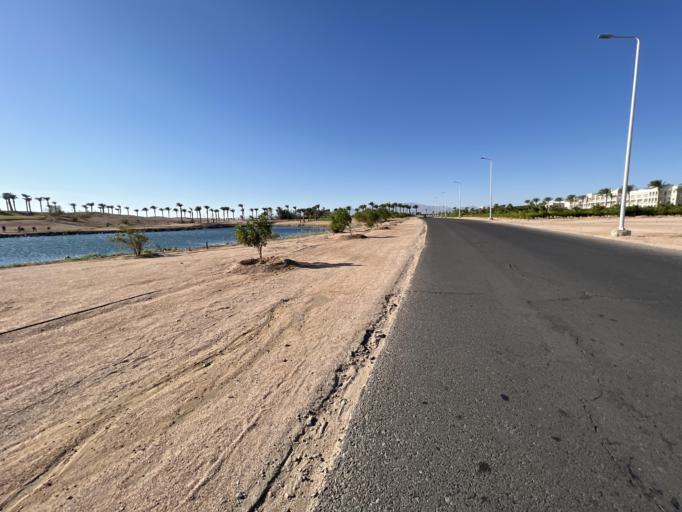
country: EG
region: Red Sea
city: Makadi Bay
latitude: 26.9824
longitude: 33.8769
